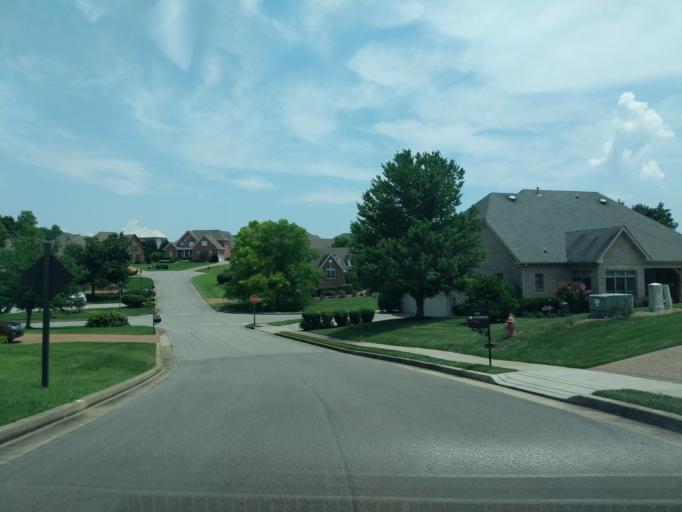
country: US
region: Tennessee
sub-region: Davidson County
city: Lakewood
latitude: 36.2313
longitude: -86.6317
